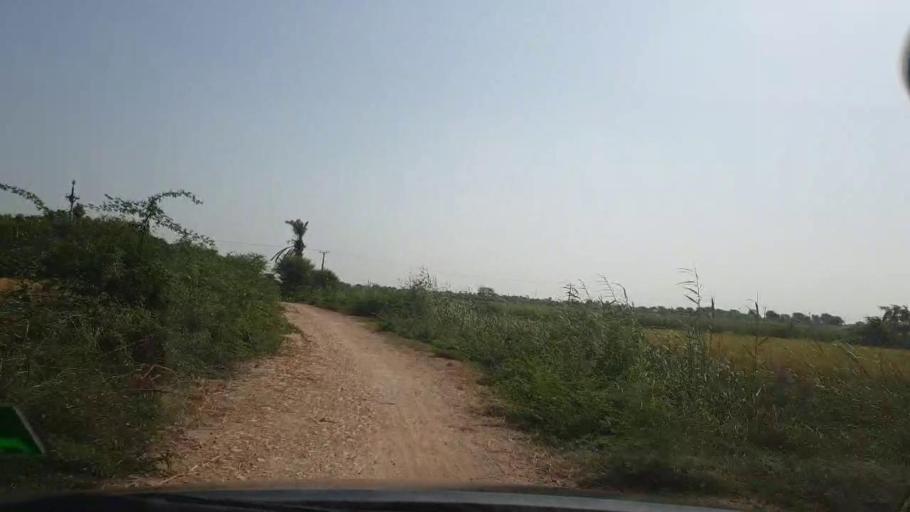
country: PK
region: Sindh
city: Tando Bago
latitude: 24.7638
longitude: 68.9447
